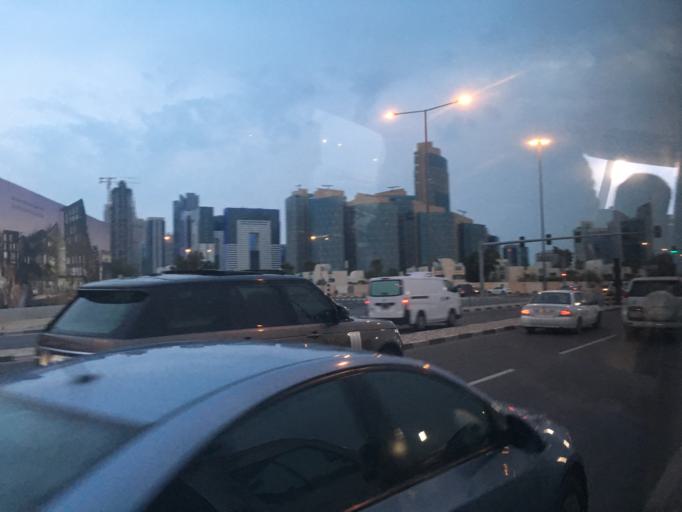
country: QA
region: Baladiyat ad Dawhah
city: Doha
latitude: 25.3204
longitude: 51.5118
